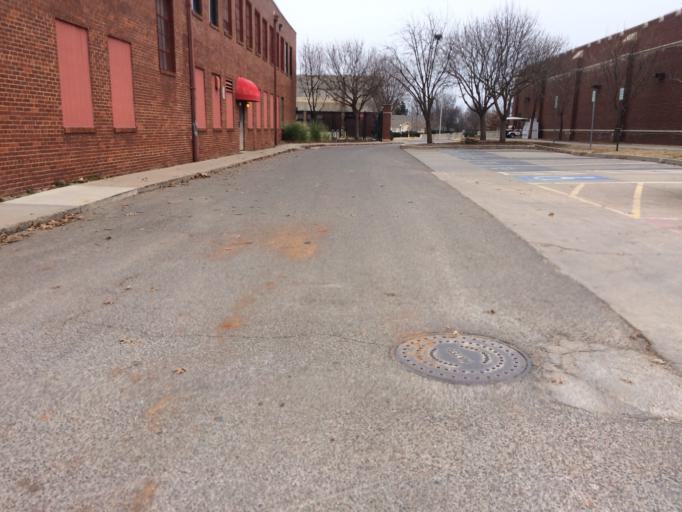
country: US
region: Oklahoma
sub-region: Cleveland County
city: Norman
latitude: 35.2087
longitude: -97.4427
